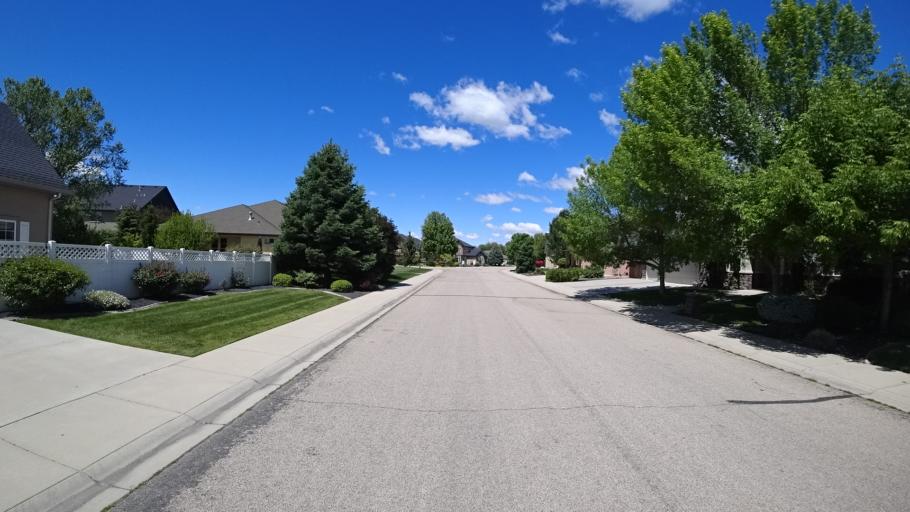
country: US
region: Idaho
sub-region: Ada County
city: Eagle
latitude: 43.6528
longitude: -116.3428
